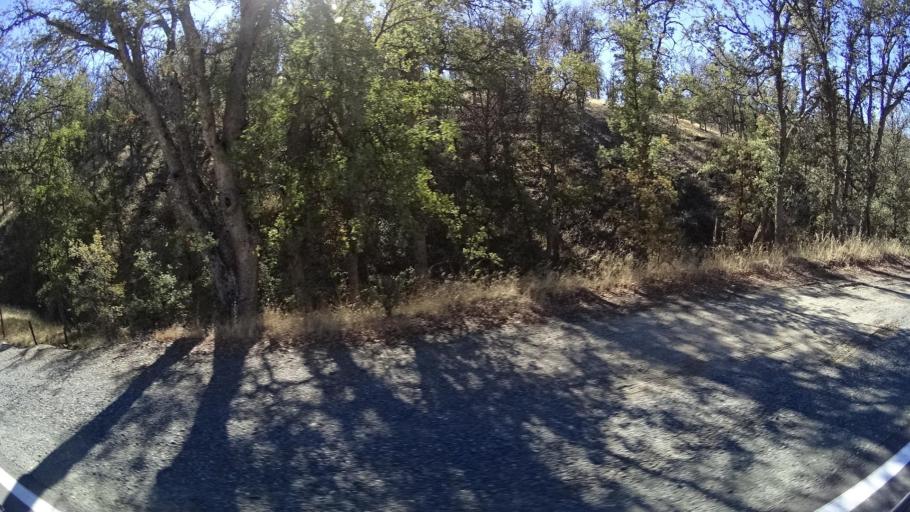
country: US
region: California
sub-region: Kern County
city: Alta Sierra
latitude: 35.7216
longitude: -118.6860
